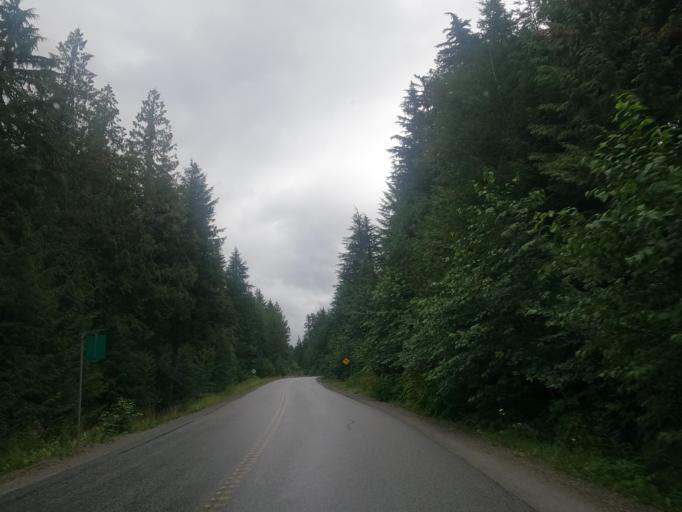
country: CA
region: British Columbia
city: Pemberton
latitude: 50.3147
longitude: -122.5661
